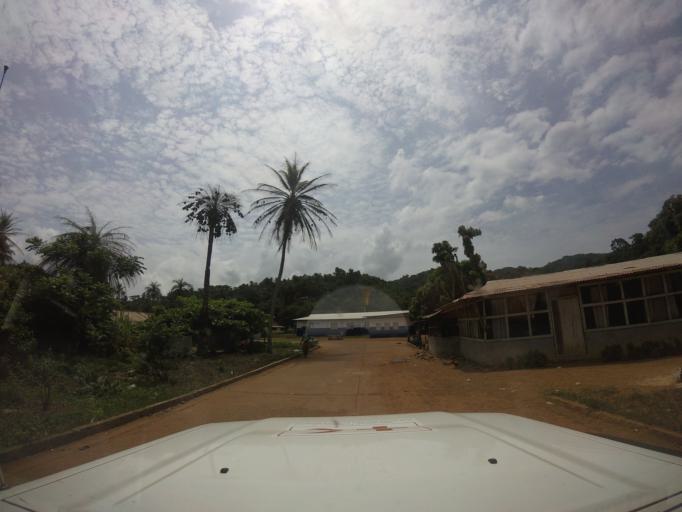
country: LR
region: Grand Cape Mount
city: Robertsport
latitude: 6.7538
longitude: -11.3730
